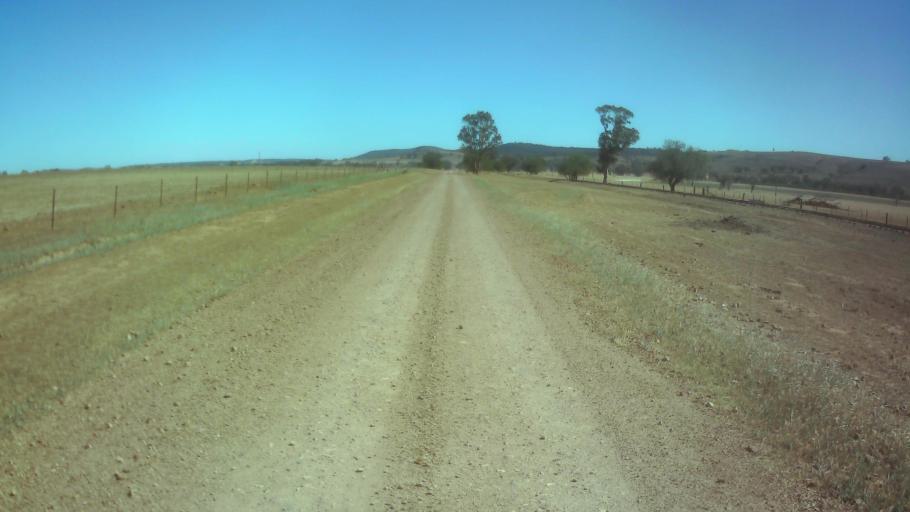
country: AU
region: New South Wales
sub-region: Weddin
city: Grenfell
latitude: -33.9586
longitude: 148.3033
